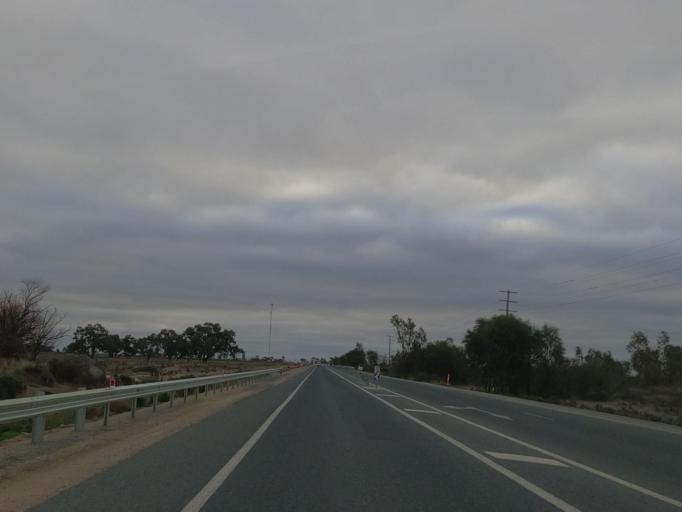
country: AU
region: Victoria
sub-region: Swan Hill
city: Swan Hill
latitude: -35.5340
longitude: 143.7433
